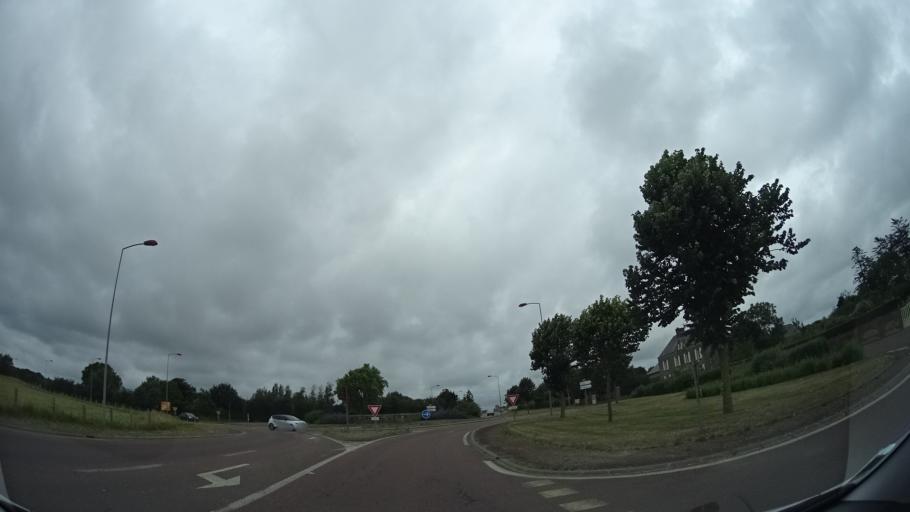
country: FR
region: Lower Normandy
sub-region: Departement de la Manche
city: Lessay
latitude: 49.2271
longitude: -1.5341
